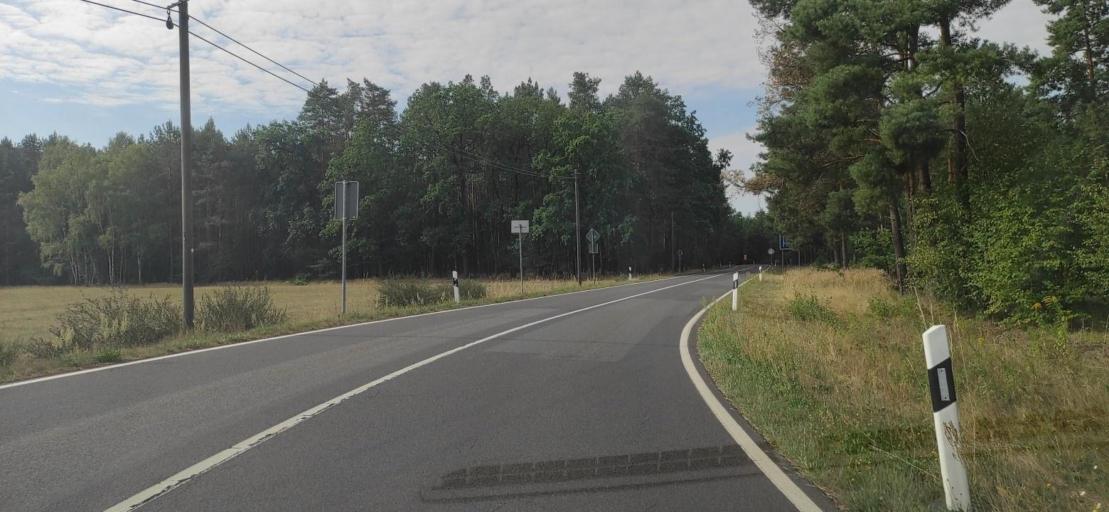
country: PL
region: Lubusz
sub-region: Powiat zarski
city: Trzebiel
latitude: 51.6712
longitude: 14.7383
